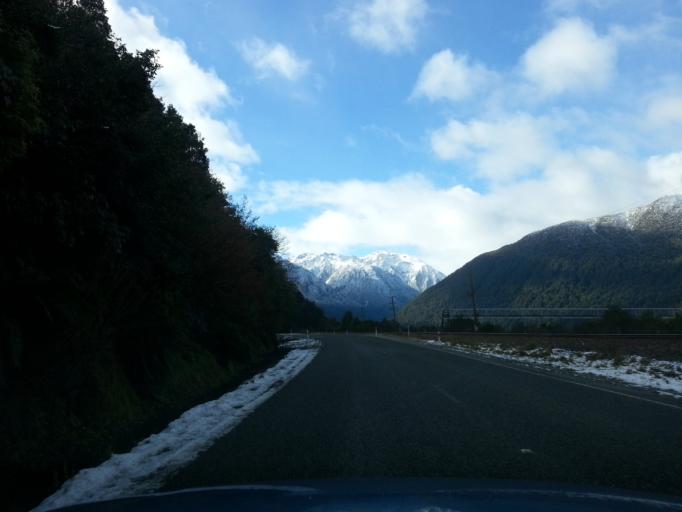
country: NZ
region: West Coast
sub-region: Grey District
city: Greymouth
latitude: -42.7881
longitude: 171.6018
